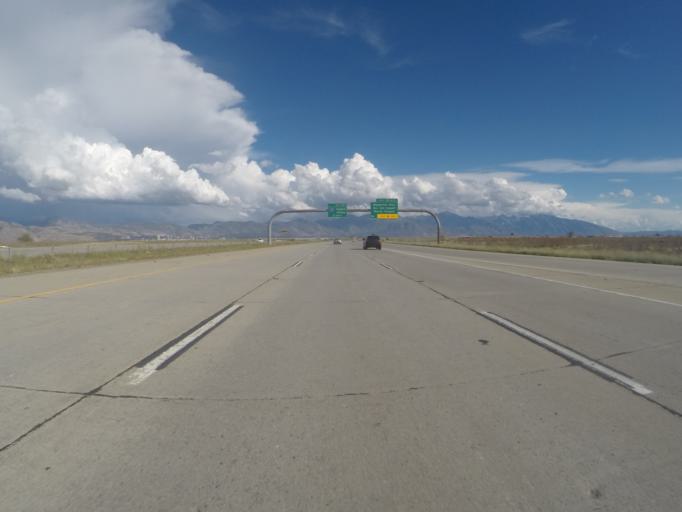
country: US
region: Utah
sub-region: Salt Lake County
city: West Valley City
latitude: 40.7687
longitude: -112.0023
